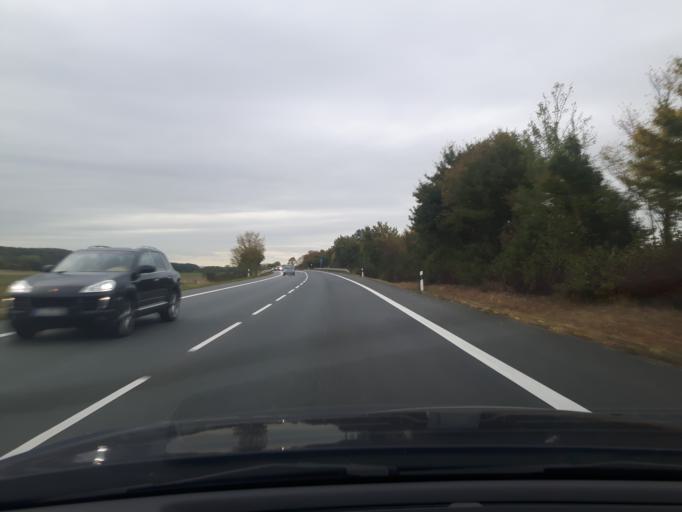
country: DE
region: Hesse
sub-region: Regierungsbezirk Giessen
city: Grossen Buseck
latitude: 50.5547
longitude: 8.7657
